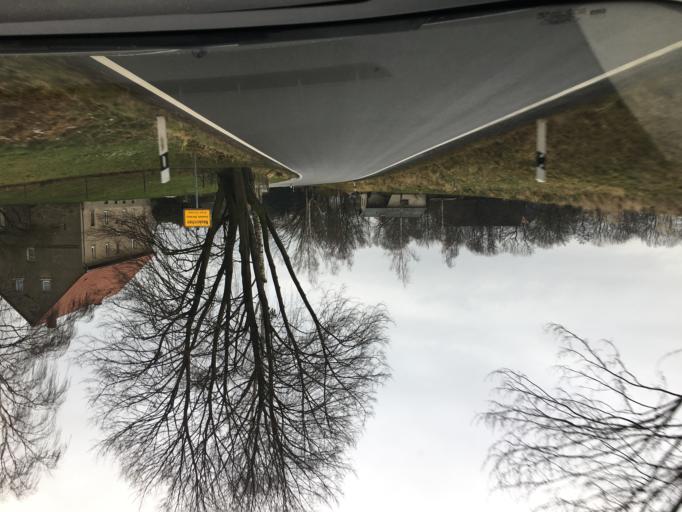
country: DE
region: Saxony
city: Pfaffroda
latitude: 50.8781
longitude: 12.5417
